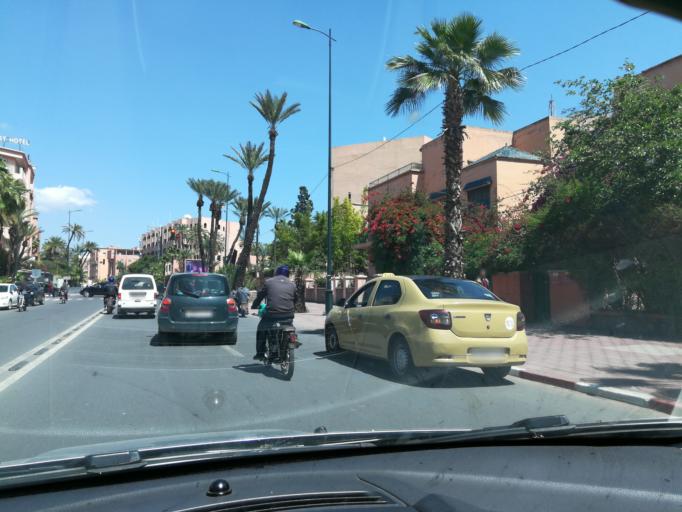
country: MA
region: Marrakech-Tensift-Al Haouz
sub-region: Marrakech
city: Marrakesh
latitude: 31.6377
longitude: -8.0097
